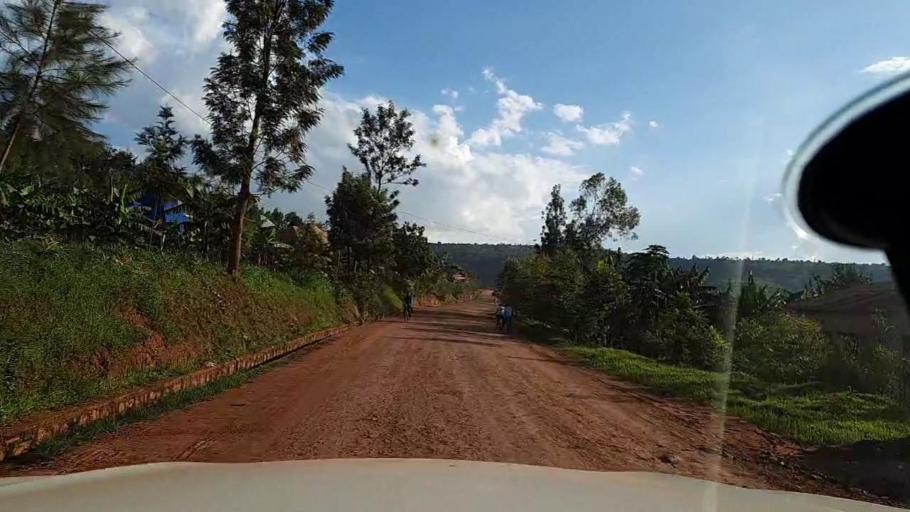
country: RW
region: Kigali
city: Kigali
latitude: -1.8981
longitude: 29.9646
